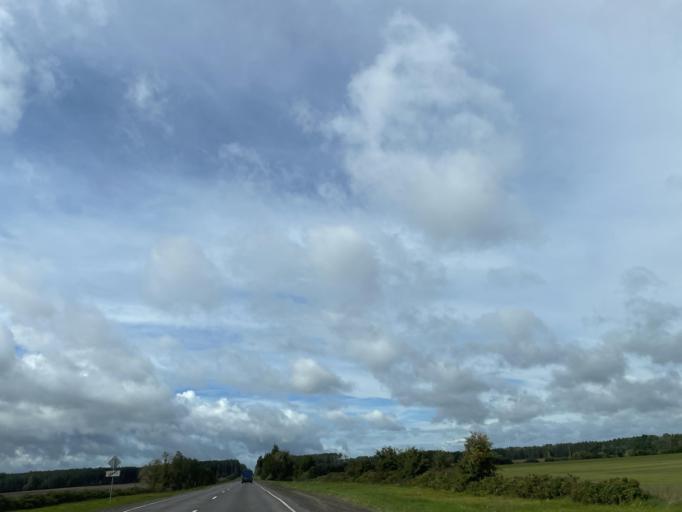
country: BY
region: Brest
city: Ivatsevichy
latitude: 52.7347
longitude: 25.2507
